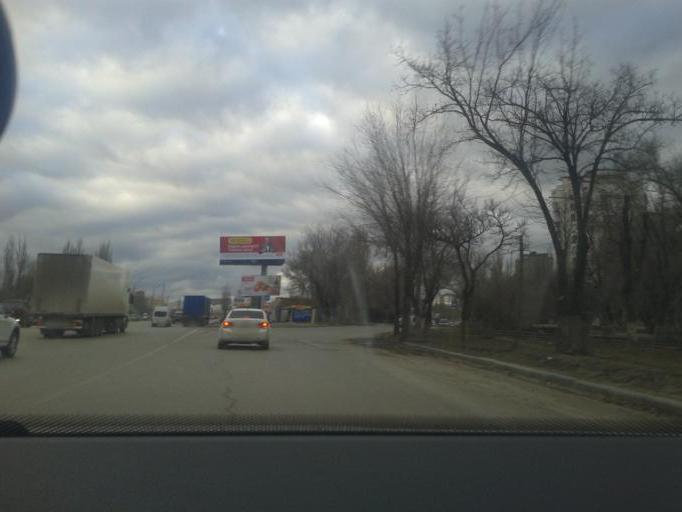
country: RU
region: Volgograd
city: Gorodishche
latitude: 48.7593
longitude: 44.4789
